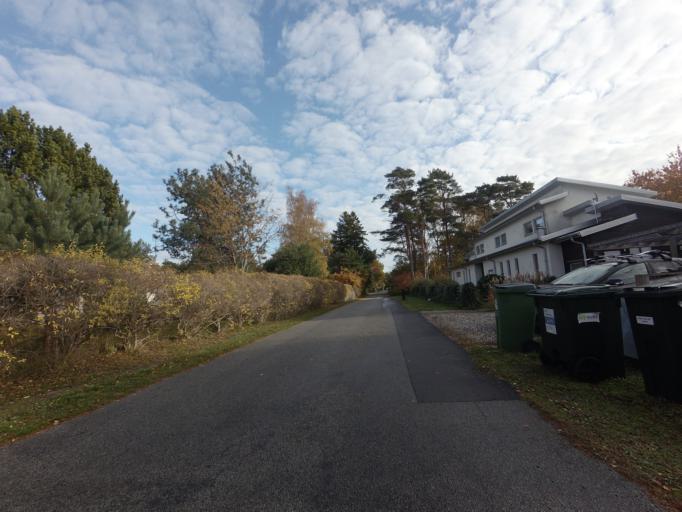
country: SE
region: Skane
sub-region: Vellinge Kommun
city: Hollviken
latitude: 55.4037
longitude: 12.9815
